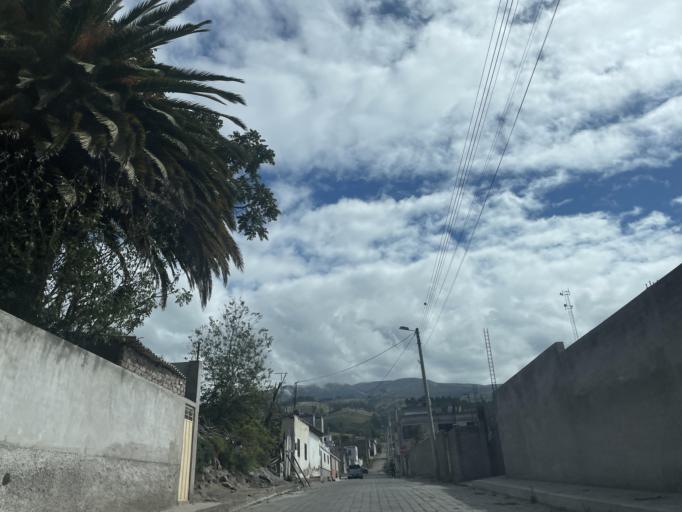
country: EC
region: Chimborazo
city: Guano
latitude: -1.6073
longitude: -78.6389
